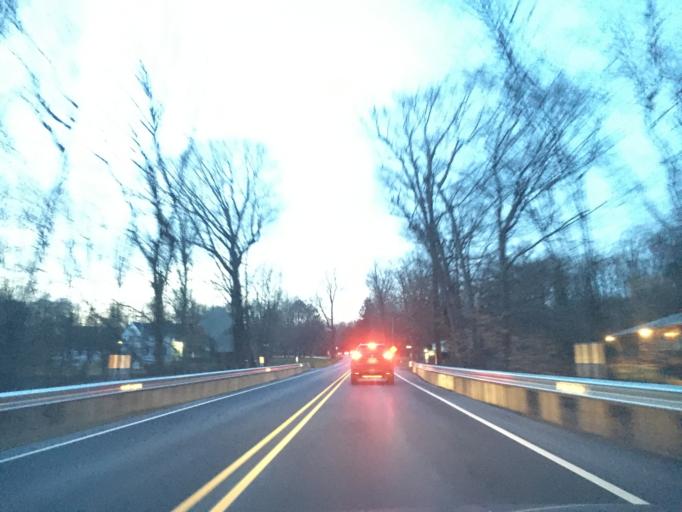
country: US
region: Pennsylvania
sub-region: Northampton County
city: Cherryville
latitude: 40.7493
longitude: -75.5230
